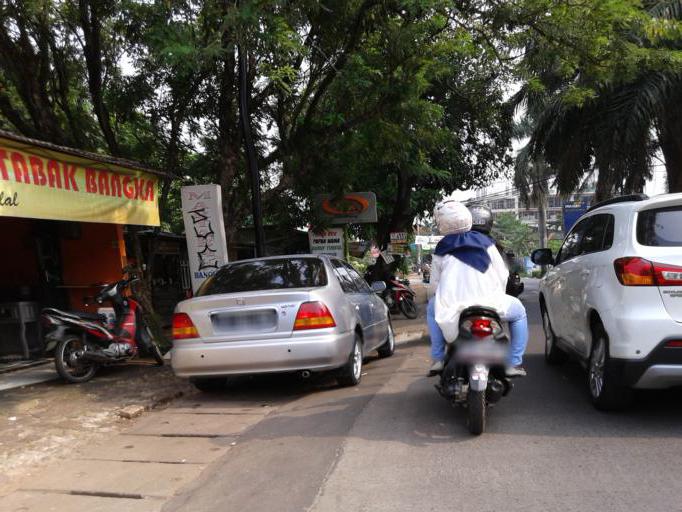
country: ID
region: West Java
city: Pamulang
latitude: -6.3196
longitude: 106.7834
